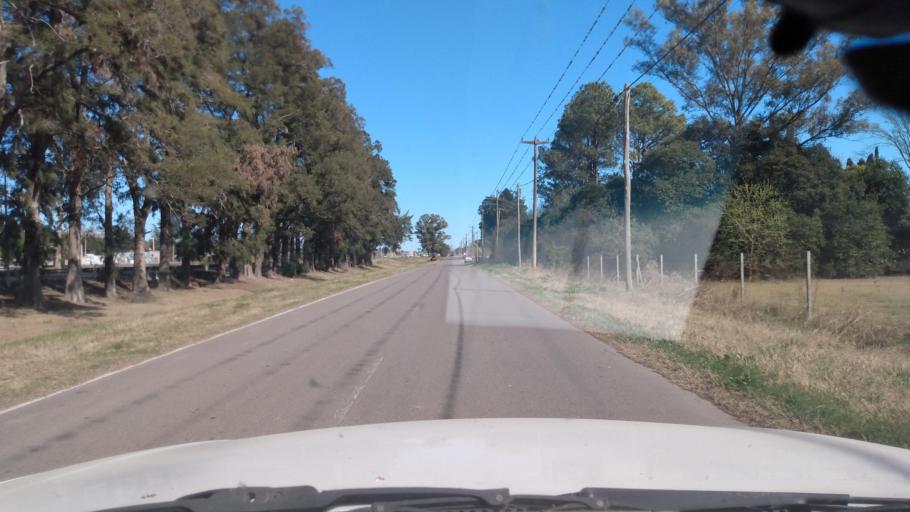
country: AR
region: Buenos Aires
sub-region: Partido de Mercedes
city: Mercedes
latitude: -34.6625
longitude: -59.3900
